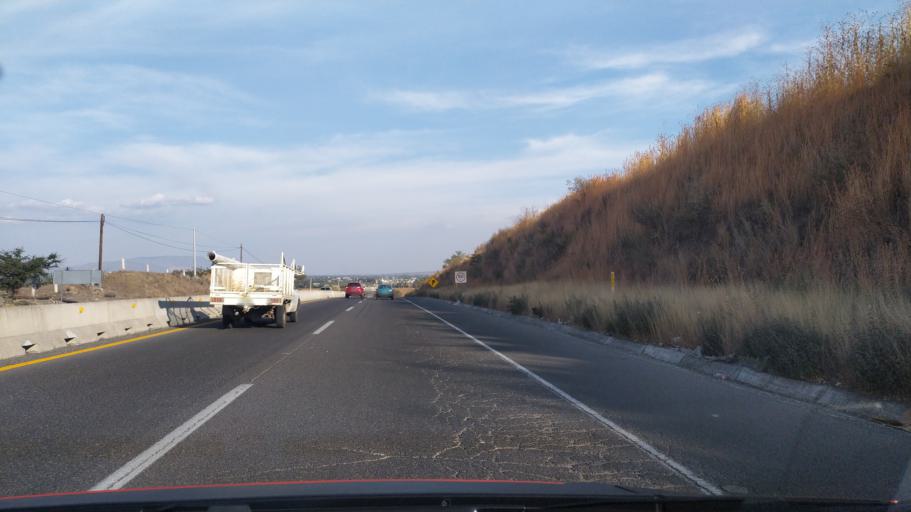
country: MX
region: Jalisco
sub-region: Poncitlan
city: Cuitzeo (La Estancia)
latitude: 20.3655
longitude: -102.8128
